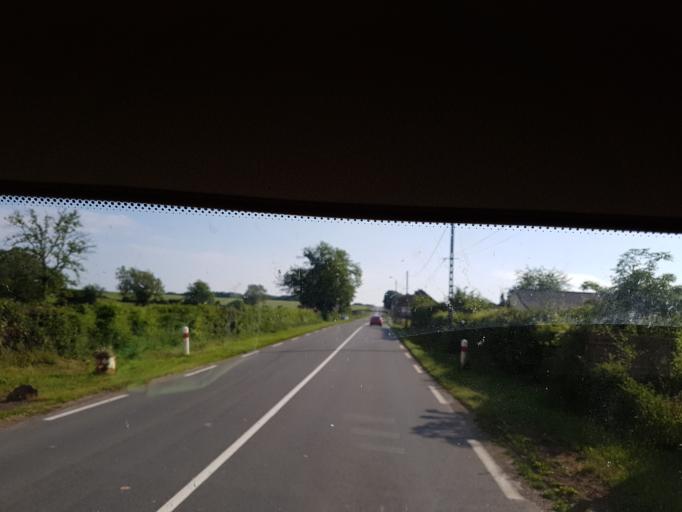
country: FR
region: Picardie
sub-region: Departement de la Somme
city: Crecy-en-Ponthieu
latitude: 50.2263
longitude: 1.9298
